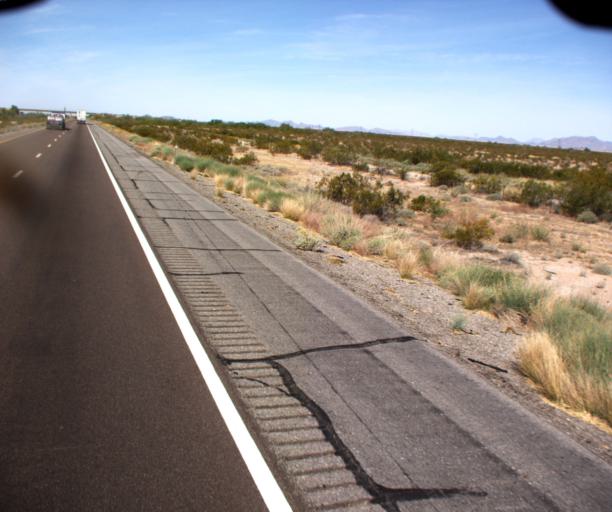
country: US
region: Arizona
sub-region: La Paz County
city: Salome
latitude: 33.5600
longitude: -113.2920
